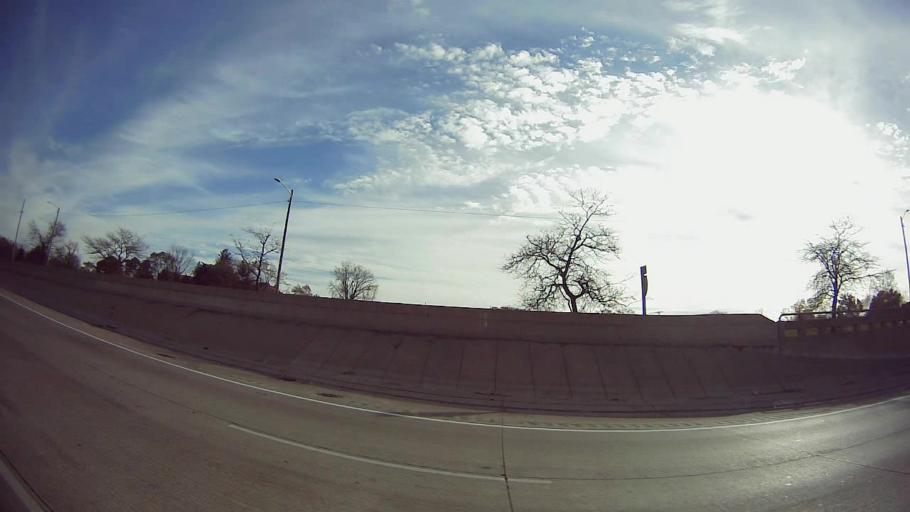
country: US
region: Michigan
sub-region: Wayne County
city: Redford
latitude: 42.3855
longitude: -83.2695
